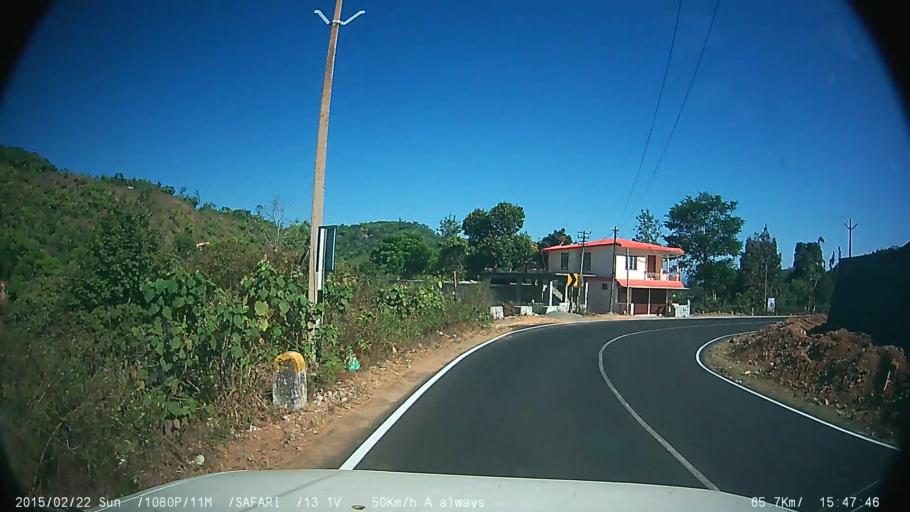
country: IN
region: Kerala
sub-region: Kottayam
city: Erattupetta
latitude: 9.5760
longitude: 76.9920
